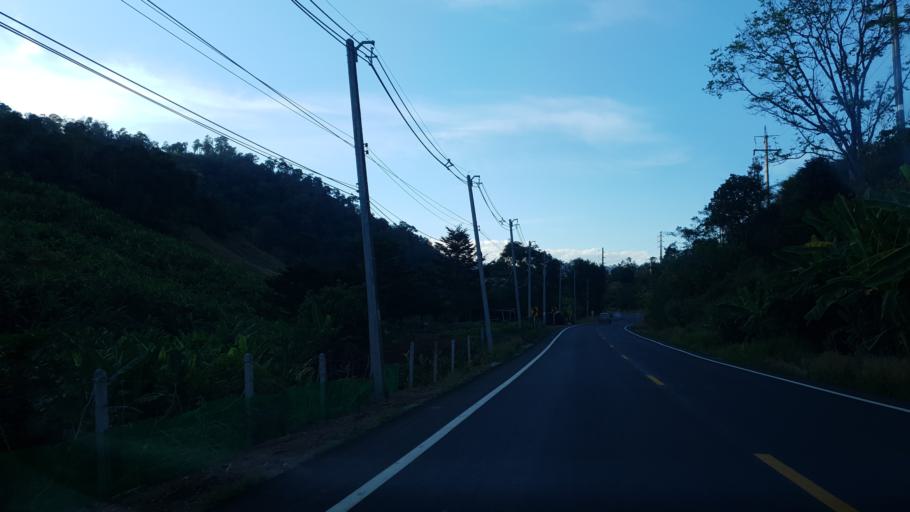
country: TH
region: Loei
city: Dan Sai
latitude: 17.2258
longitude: 101.0610
